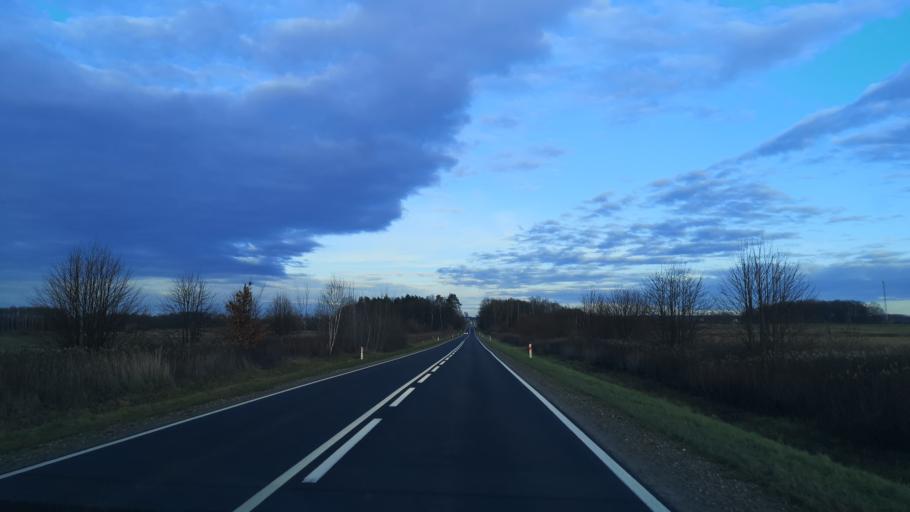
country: PL
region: Subcarpathian Voivodeship
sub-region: Powiat przeworski
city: Adamowka
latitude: 50.2456
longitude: 22.6783
